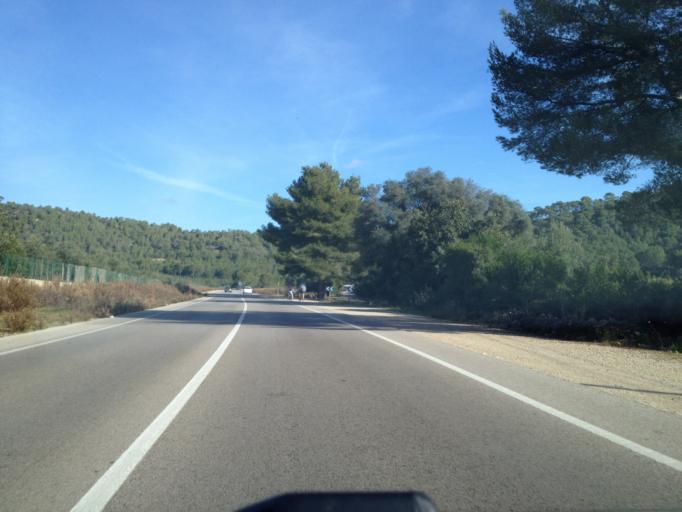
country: ES
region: Balearic Islands
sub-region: Illes Balears
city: Arta
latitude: 39.6627
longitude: 3.3928
